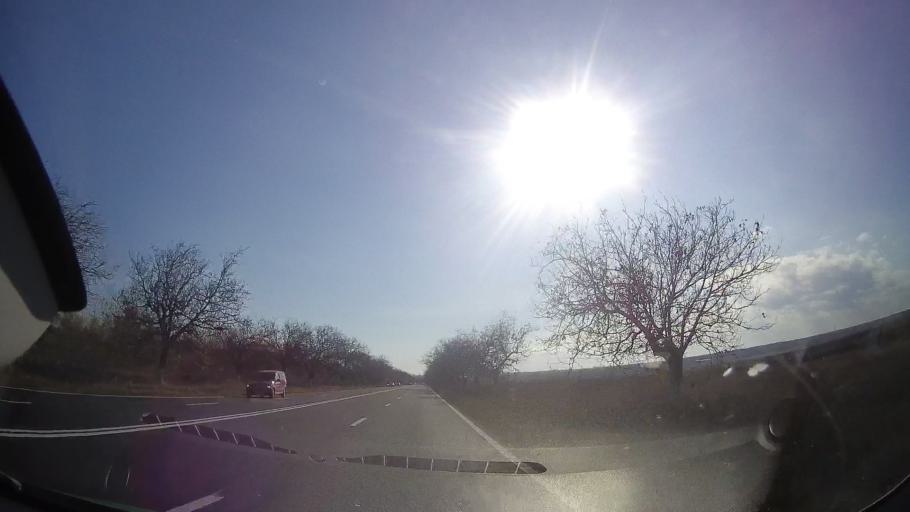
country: RO
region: Constanta
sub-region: Municipiul Mangalia
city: Mangalia
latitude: 43.8542
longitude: 28.5760
